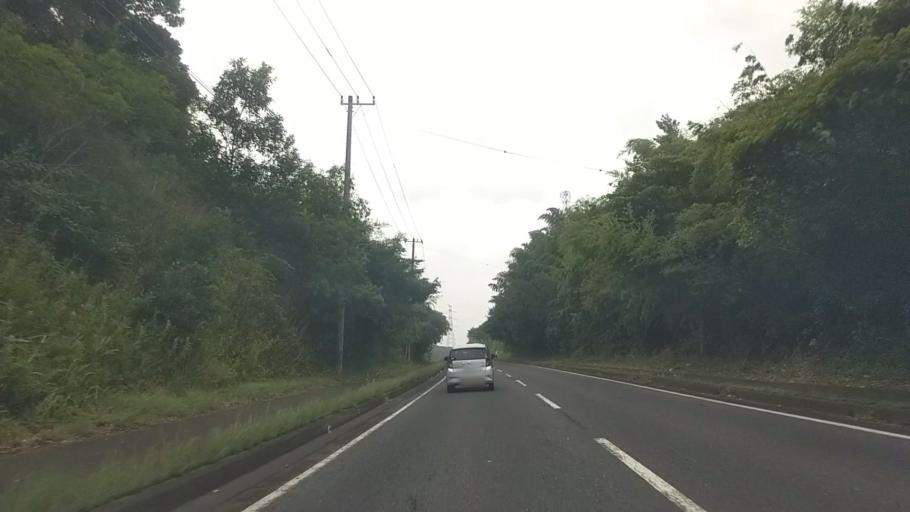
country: JP
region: Chiba
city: Kisarazu
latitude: 35.3881
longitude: 139.9915
